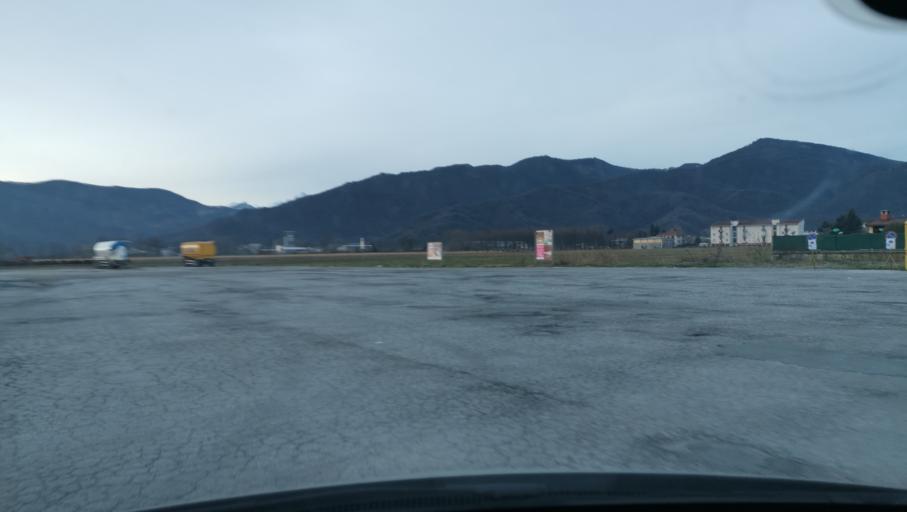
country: IT
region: Piedmont
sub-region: Provincia di Cuneo
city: Caraglio
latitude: 44.4141
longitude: 7.4360
